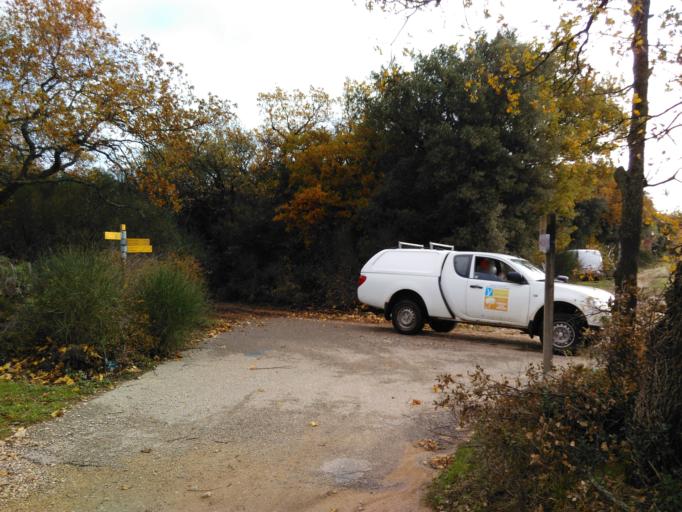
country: FR
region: Rhone-Alpes
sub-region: Departement de la Drome
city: Rochegude
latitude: 44.2263
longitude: 4.8239
